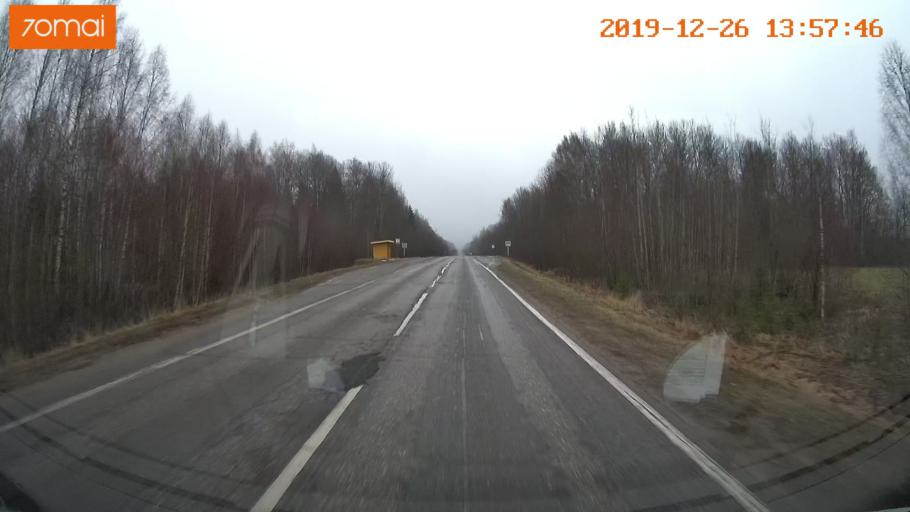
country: RU
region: Jaroslavl
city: Poshekhon'ye
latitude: 58.5795
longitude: 38.6866
